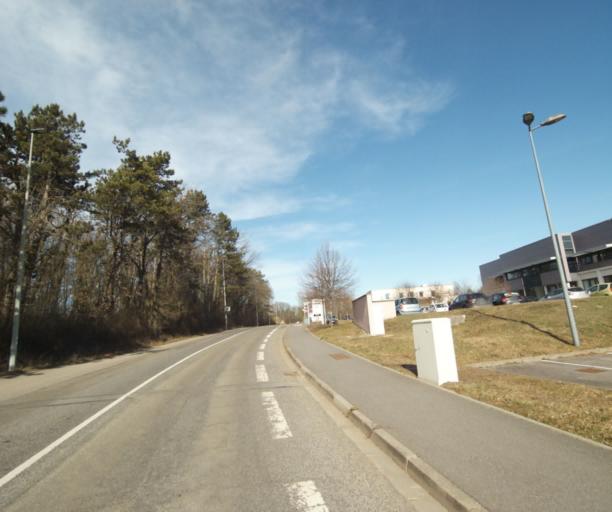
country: FR
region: Lorraine
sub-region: Departement de Meurthe-et-Moselle
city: Villers-les-Nancy
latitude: 48.6586
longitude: 6.1284
